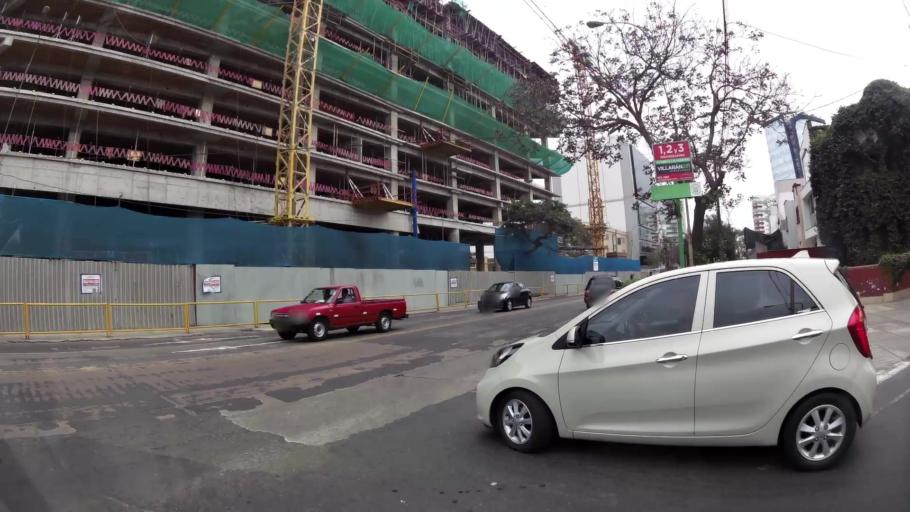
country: PE
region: Lima
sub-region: Lima
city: Surco
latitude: -12.1303
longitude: -77.0207
